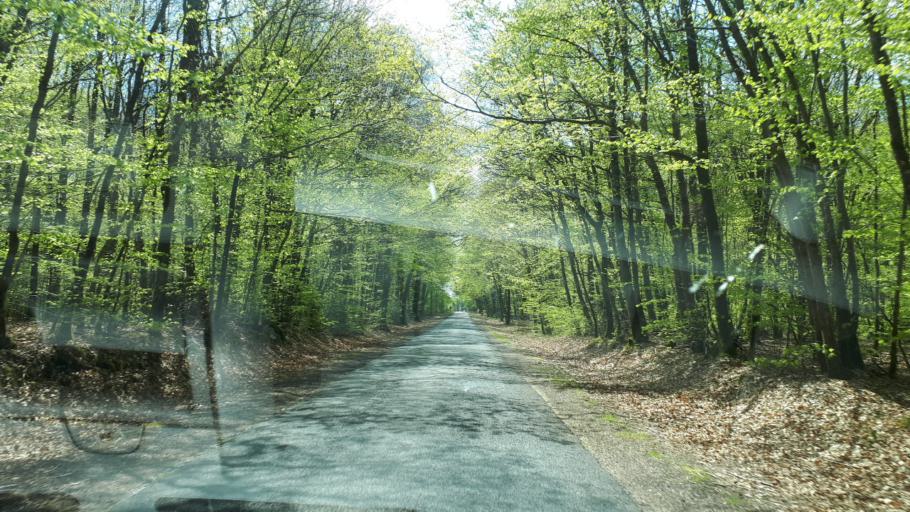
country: FR
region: Centre
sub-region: Departement du Cher
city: Henrichemont
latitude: 47.2896
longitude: 2.5772
